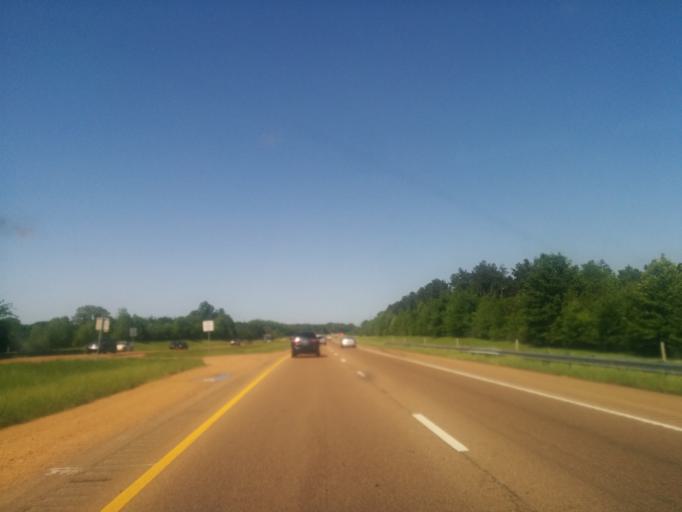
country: US
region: Mississippi
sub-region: Madison County
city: Madison
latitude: 32.4964
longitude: -90.1231
